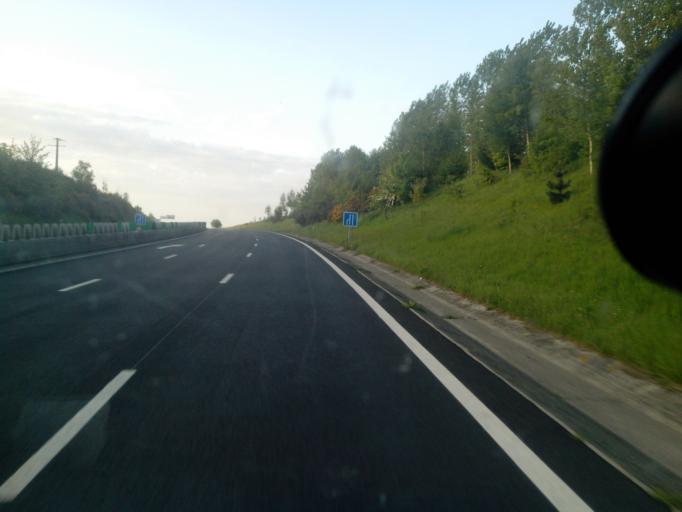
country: FR
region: Picardie
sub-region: Departement de la Somme
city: Bouttencourt
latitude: 49.9475
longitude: 1.6448
